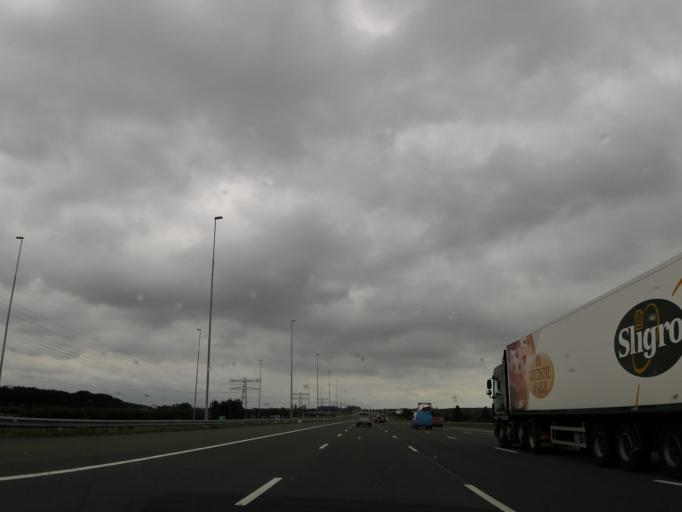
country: NL
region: Utrecht
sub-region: Stichtse Vecht
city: Breukelen
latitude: 52.1588
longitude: 4.9917
